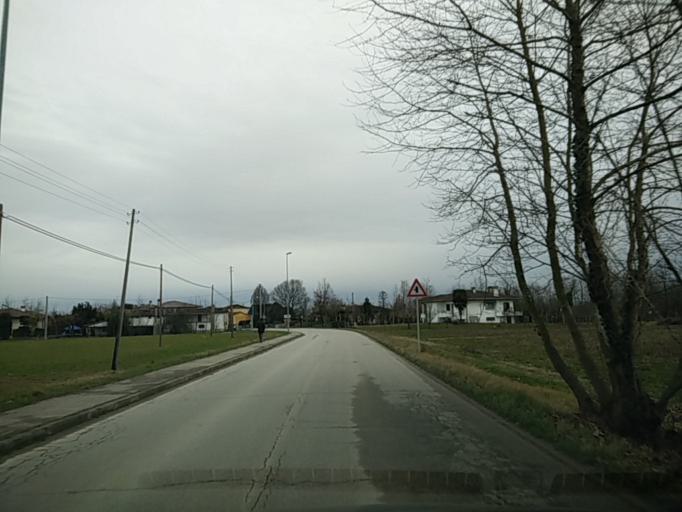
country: IT
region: Veneto
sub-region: Provincia di Treviso
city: Ca' Rainati
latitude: 45.7510
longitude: 11.8682
